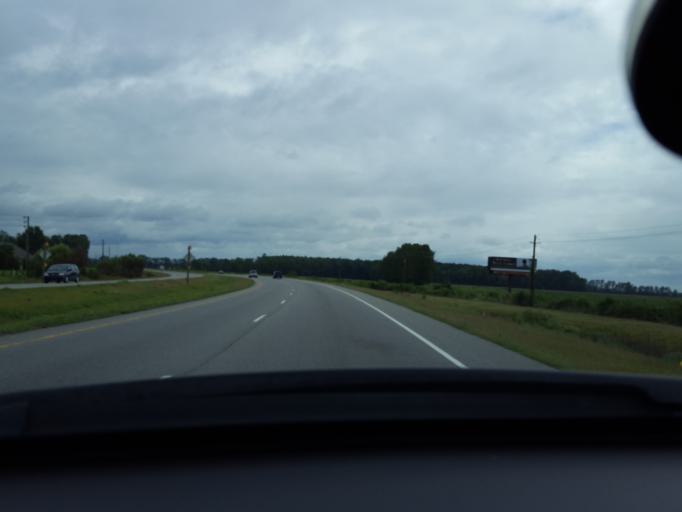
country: US
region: North Carolina
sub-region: Pitt County
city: Ayden
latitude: 35.4660
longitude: -77.4359
